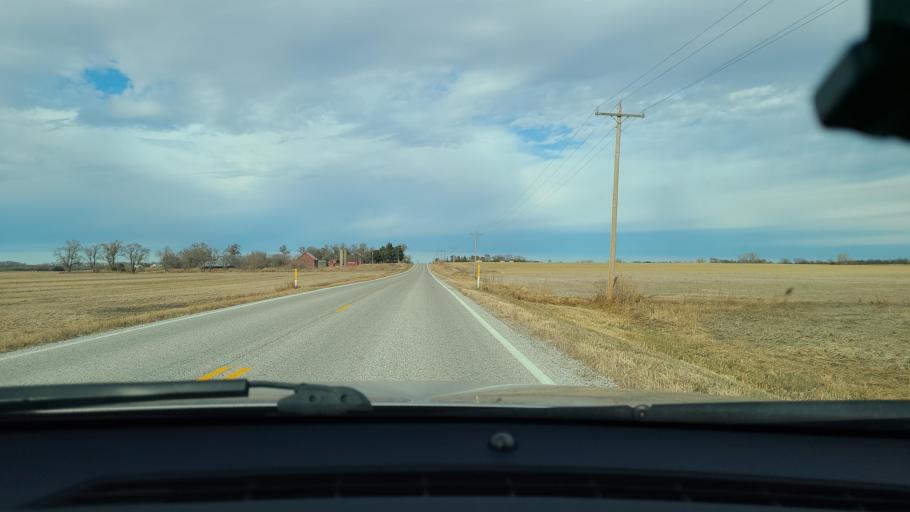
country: US
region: Kansas
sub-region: McPherson County
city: Inman
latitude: 38.2910
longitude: -97.9250
